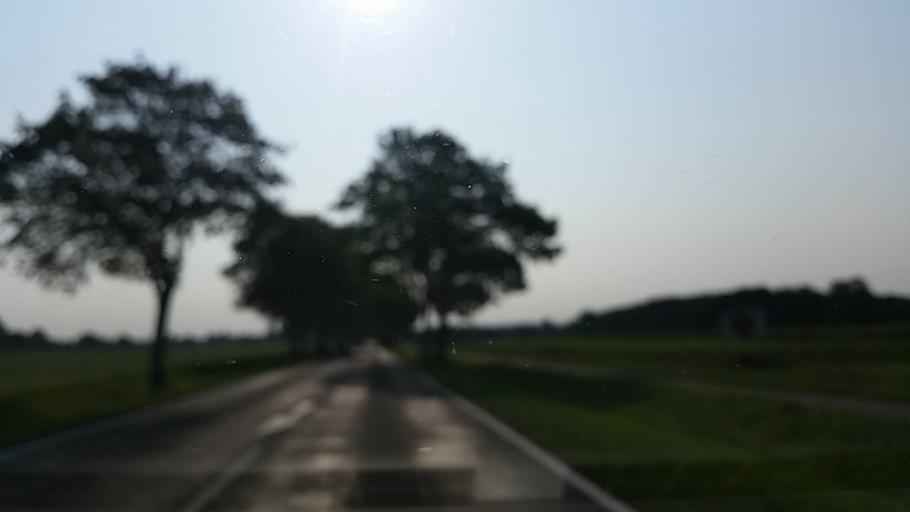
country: DE
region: Mecklenburg-Vorpommern
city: Hagenow
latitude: 53.4711
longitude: 11.1486
